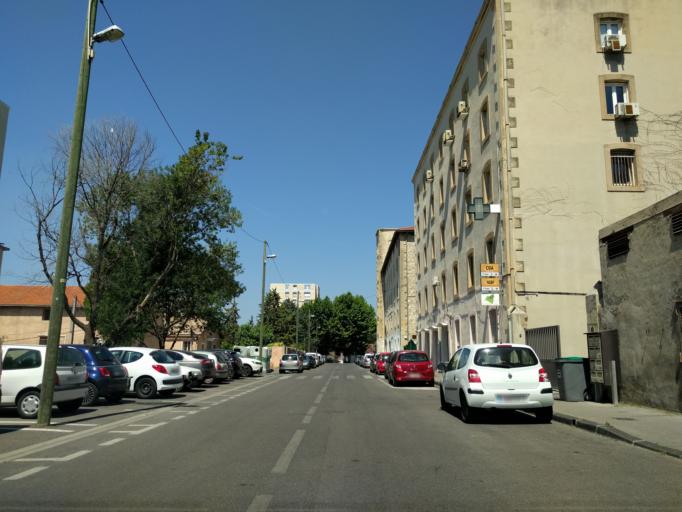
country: FR
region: Provence-Alpes-Cote d'Azur
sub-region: Departement des Bouches-du-Rhone
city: Marseille 13
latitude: 43.3193
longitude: 5.4009
